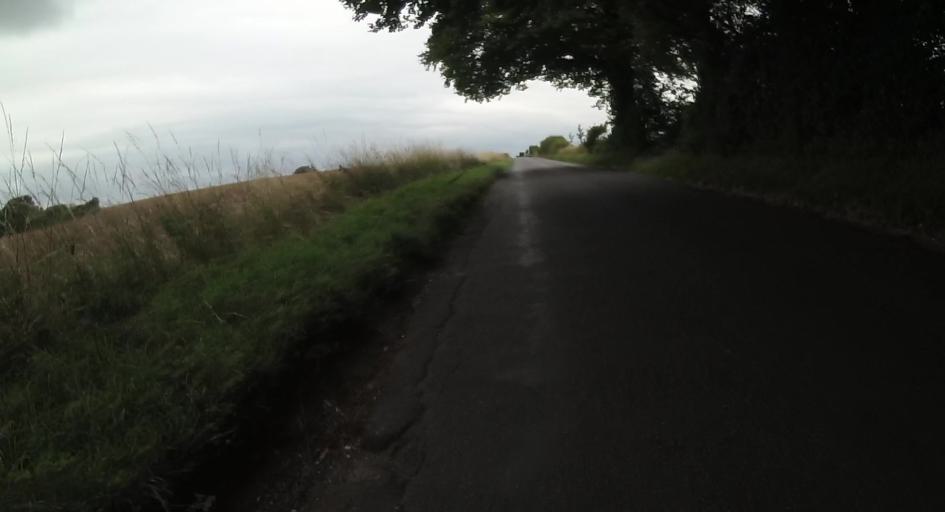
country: GB
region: England
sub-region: Hampshire
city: Bishops Waltham
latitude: 51.0291
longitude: -1.2081
